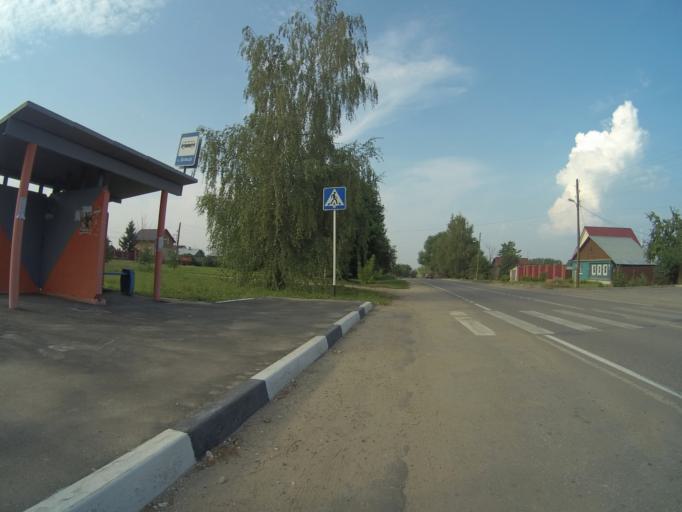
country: RU
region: Vladimir
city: Suzdal'
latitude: 56.4289
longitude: 40.4175
